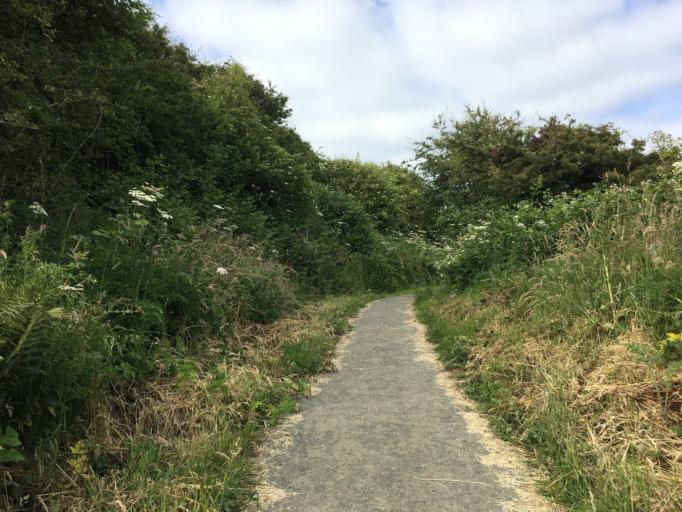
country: GB
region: England
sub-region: Northumberland
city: Alnmouth
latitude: 55.4418
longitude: -1.5930
